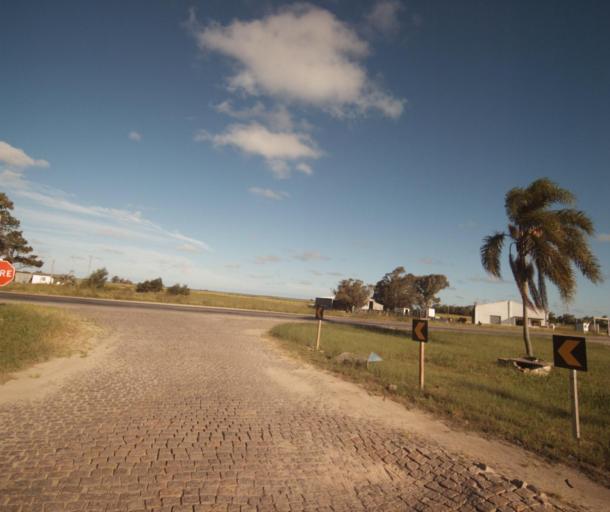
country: BR
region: Rio Grande do Sul
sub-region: Arroio Grande
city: Arroio Grande
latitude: -32.8536
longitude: -52.7041
